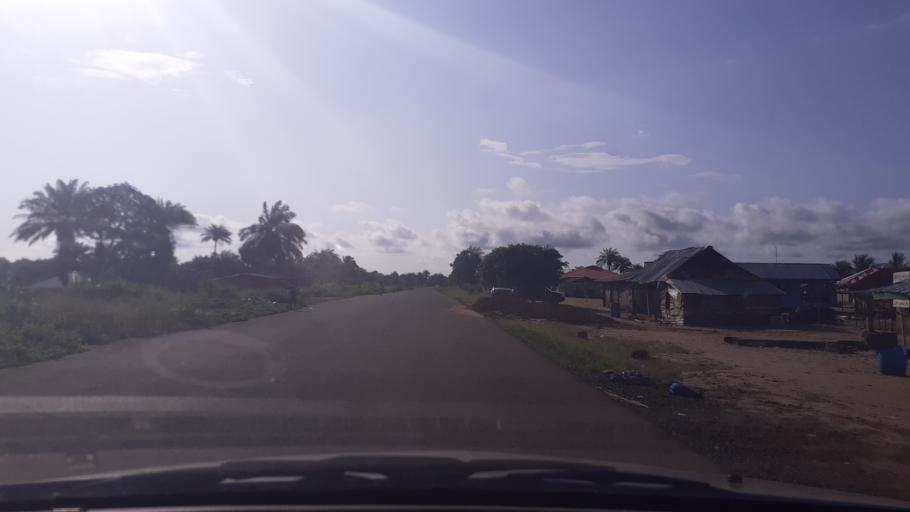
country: LR
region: Montserrado
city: Bensonville City
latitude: 6.1687
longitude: -10.4461
